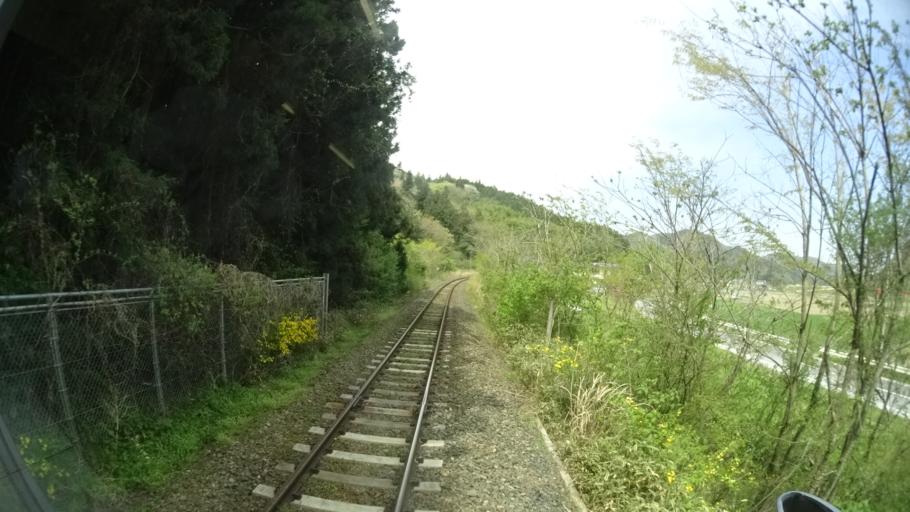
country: JP
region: Iwate
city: Ichinoseki
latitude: 38.9576
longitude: 141.2469
